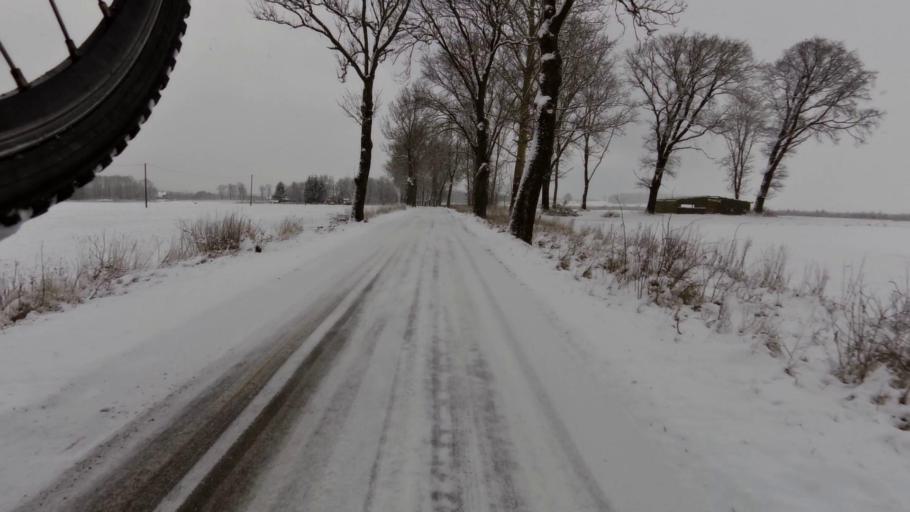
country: PL
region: West Pomeranian Voivodeship
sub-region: Powiat bialogardzki
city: Bialogard
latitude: 53.9657
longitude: 15.9740
